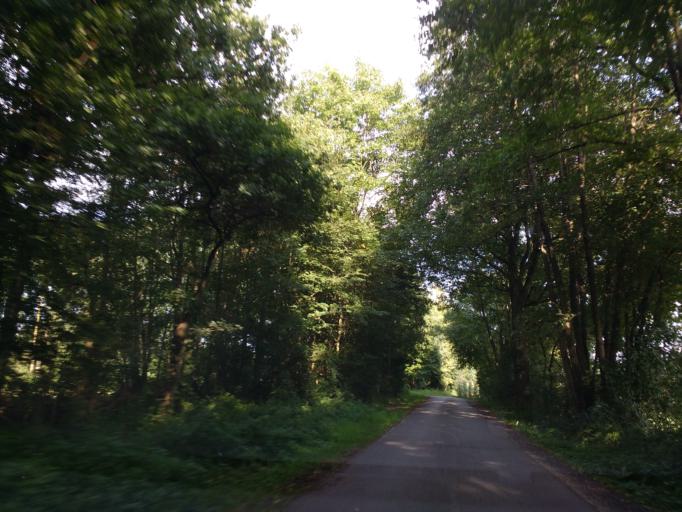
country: DE
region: North Rhine-Westphalia
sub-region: Regierungsbezirk Detmold
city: Hovelhof
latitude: 51.7732
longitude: 8.6247
